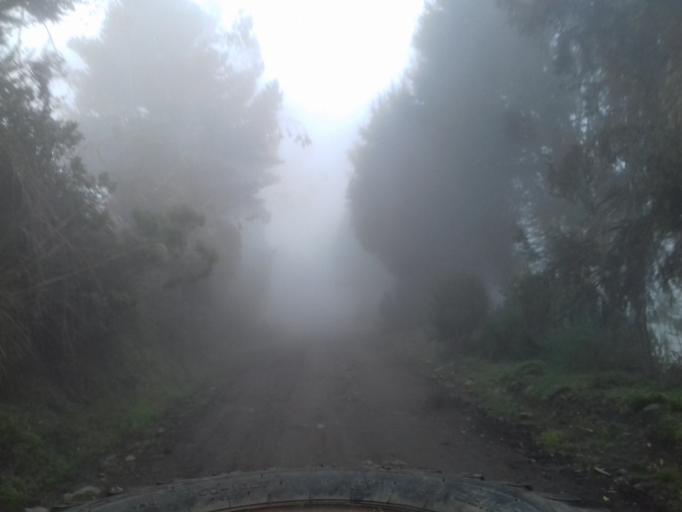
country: CO
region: Tolima
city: Murillo
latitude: 4.9048
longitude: -75.2510
